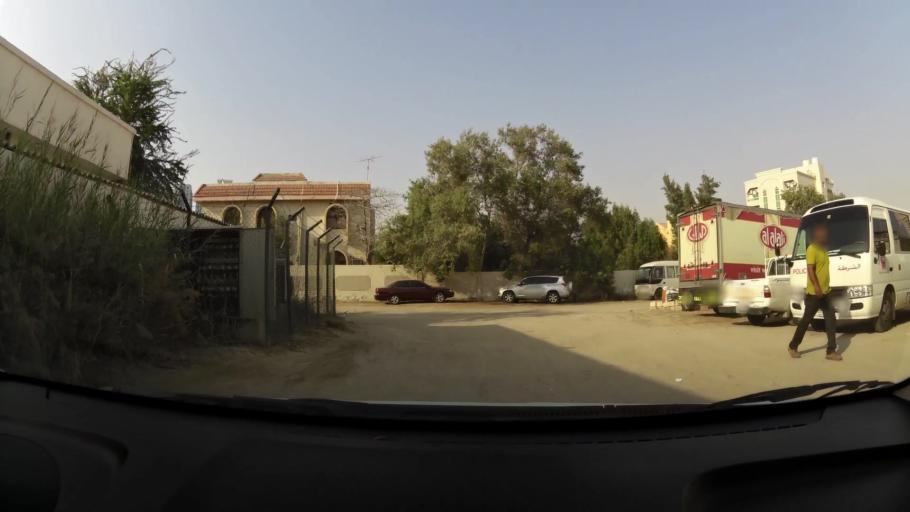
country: AE
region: Ajman
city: Ajman
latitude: 25.3866
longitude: 55.4406
